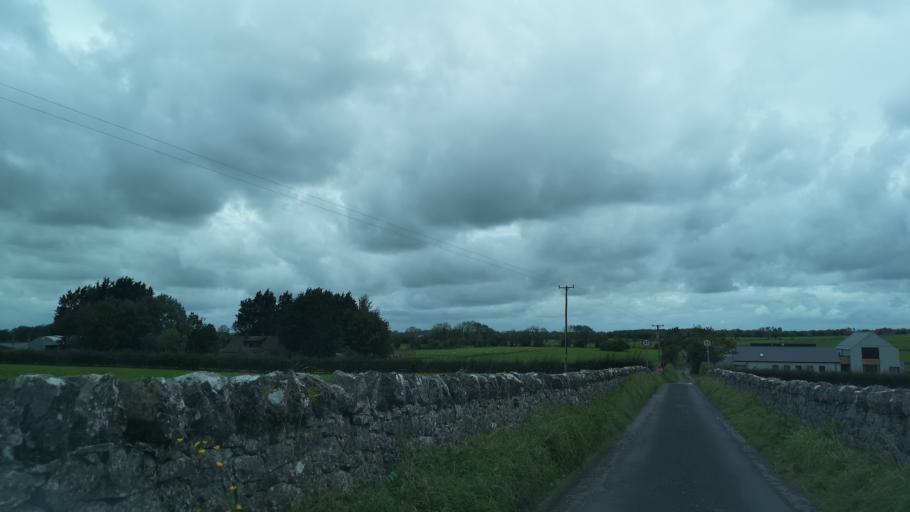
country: IE
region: Connaught
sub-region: County Galway
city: Athenry
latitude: 53.3132
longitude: -8.7464
